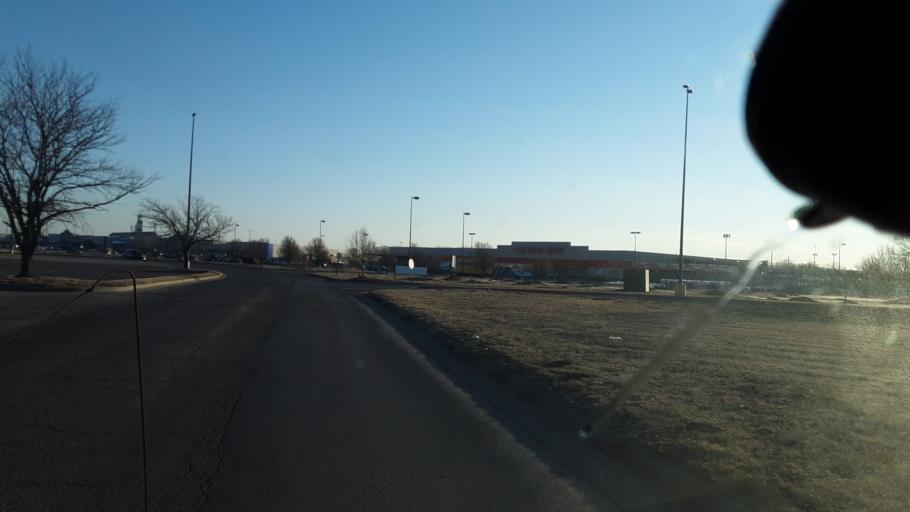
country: US
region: Kansas
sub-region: Reno County
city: Hutchinson
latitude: 38.0670
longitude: -97.8959
